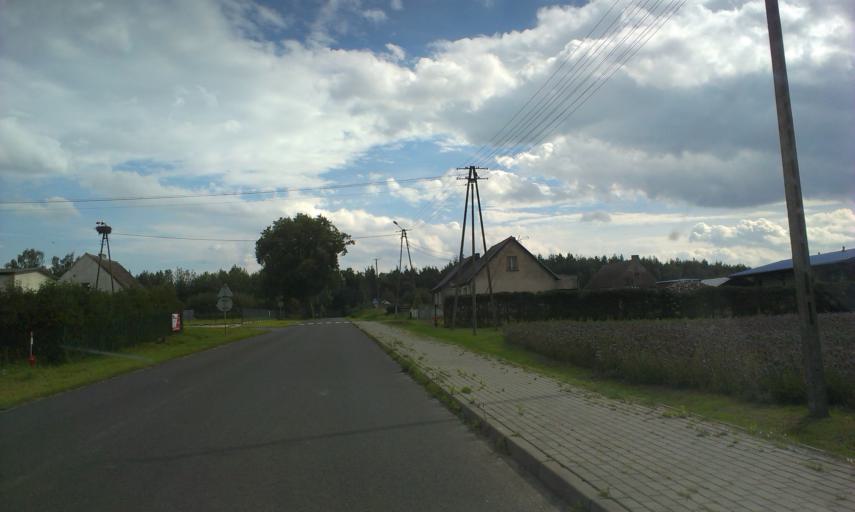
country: PL
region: Greater Poland Voivodeship
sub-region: Powiat zlotowski
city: Zlotow
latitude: 53.4421
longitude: 16.9848
